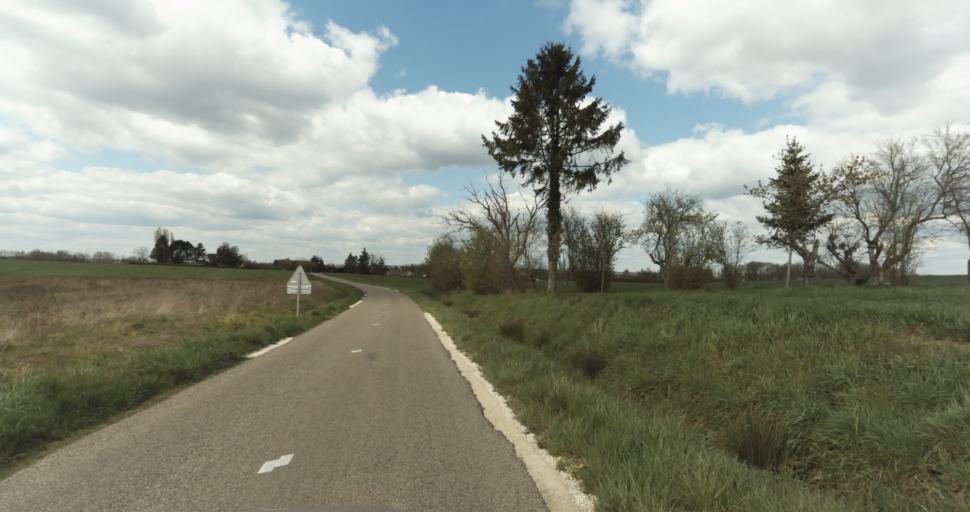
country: FR
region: Bourgogne
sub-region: Departement de la Cote-d'Or
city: Auxonne
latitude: 47.1839
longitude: 5.4104
